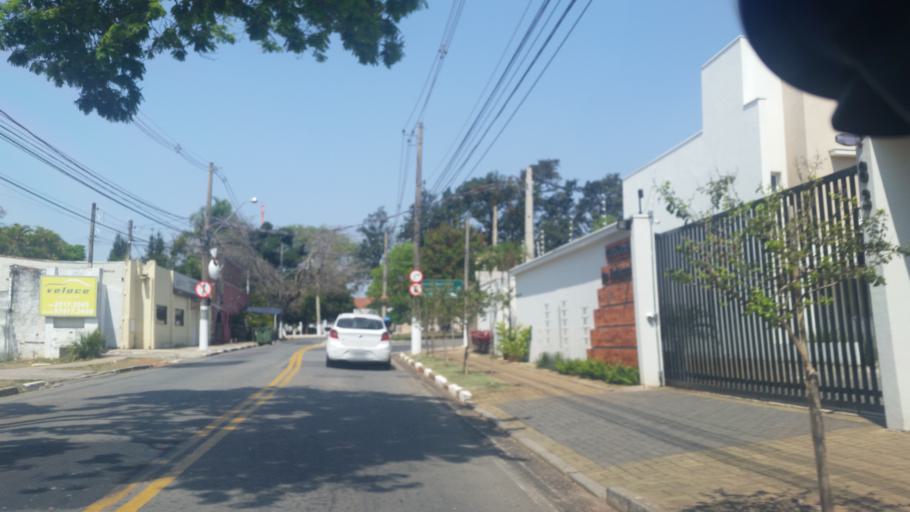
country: BR
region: Sao Paulo
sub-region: Campinas
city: Campinas
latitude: -22.8634
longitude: -47.0527
